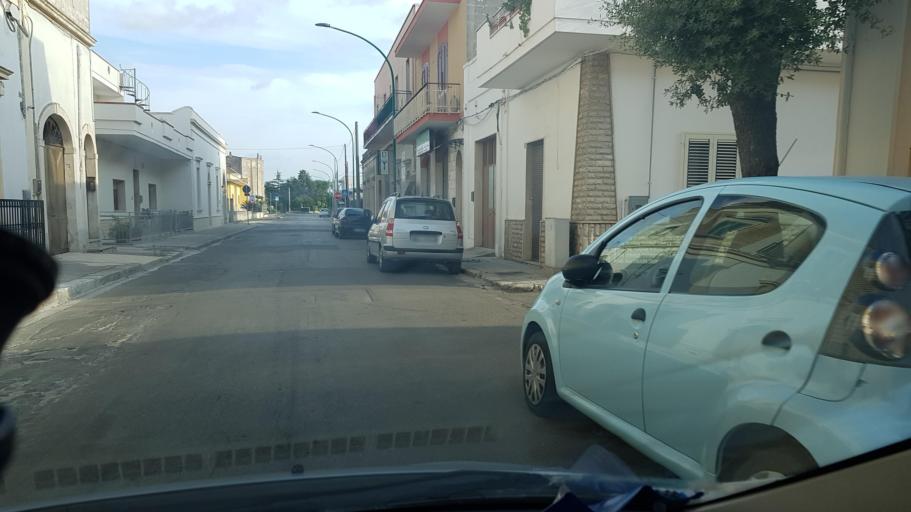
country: IT
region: Apulia
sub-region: Provincia di Lecce
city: Veglie
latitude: 40.3318
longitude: 17.9721
